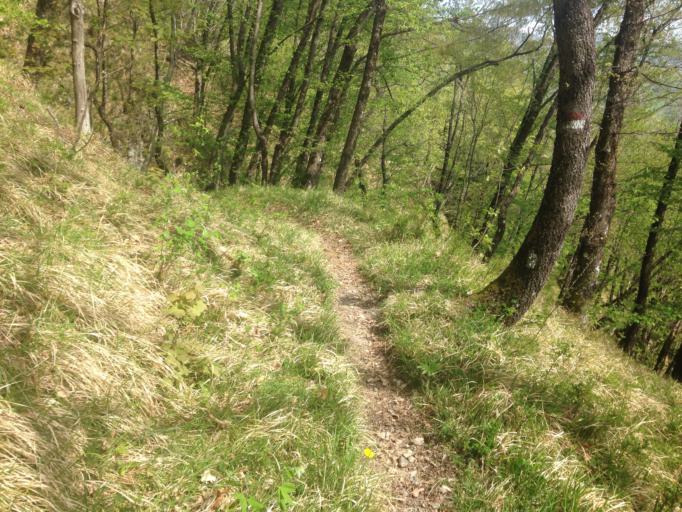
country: IT
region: Emilia-Romagna
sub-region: Provincia di Bologna
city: Lizzano in Belvedere
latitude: 44.1588
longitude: 10.8924
